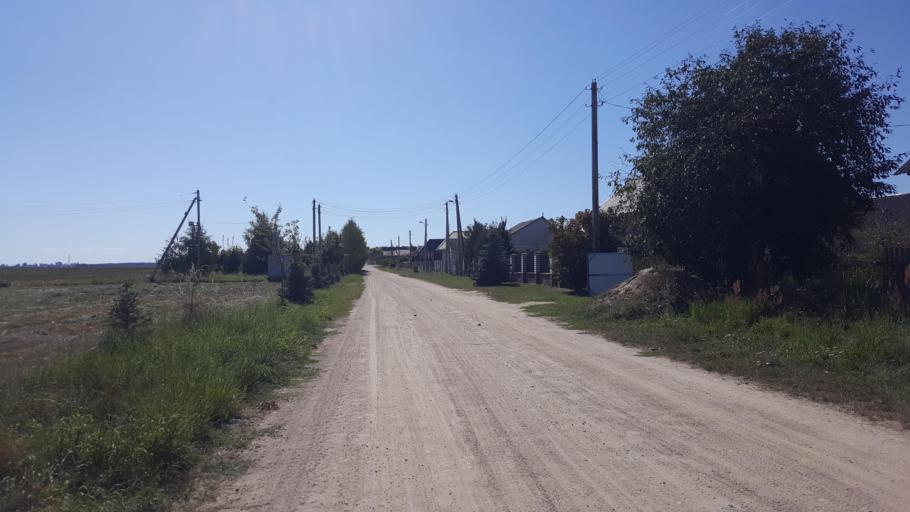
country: BY
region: Brest
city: Vysokaye
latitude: 52.2623
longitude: 23.5027
